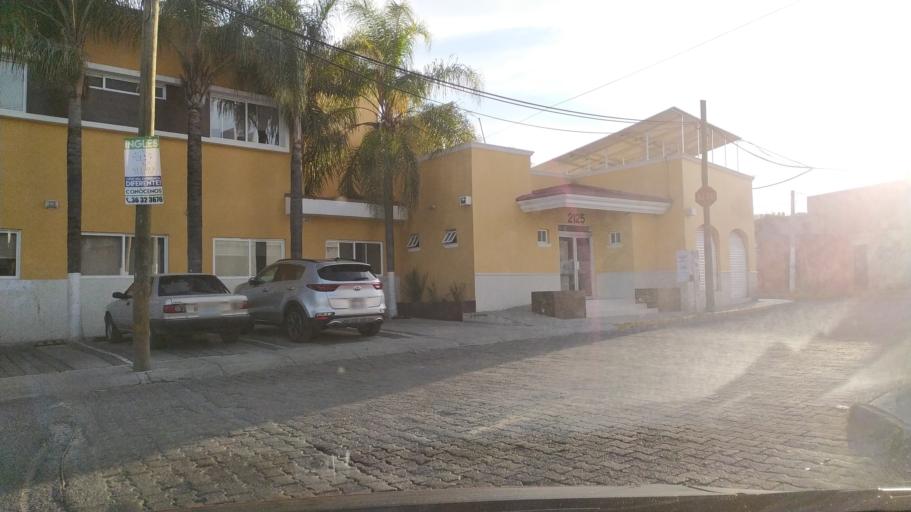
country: MX
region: Jalisco
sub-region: Tlajomulco de Zuniga
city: Palomar
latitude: 20.6253
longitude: -103.4555
